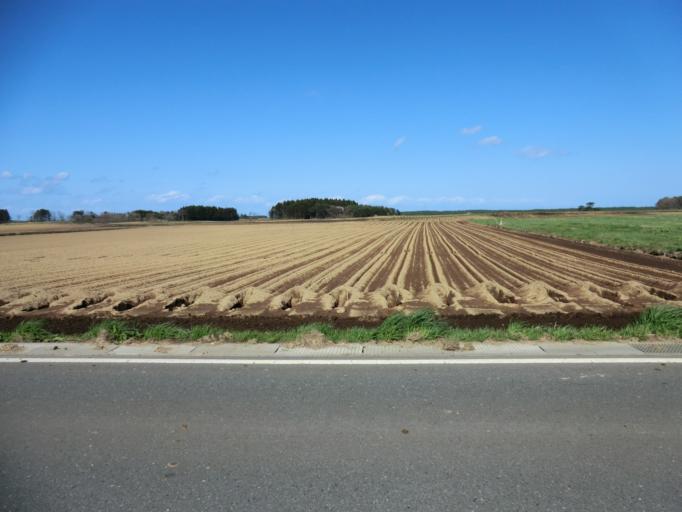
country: JP
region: Aomori
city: Misawa
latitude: 40.8580
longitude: 141.3595
